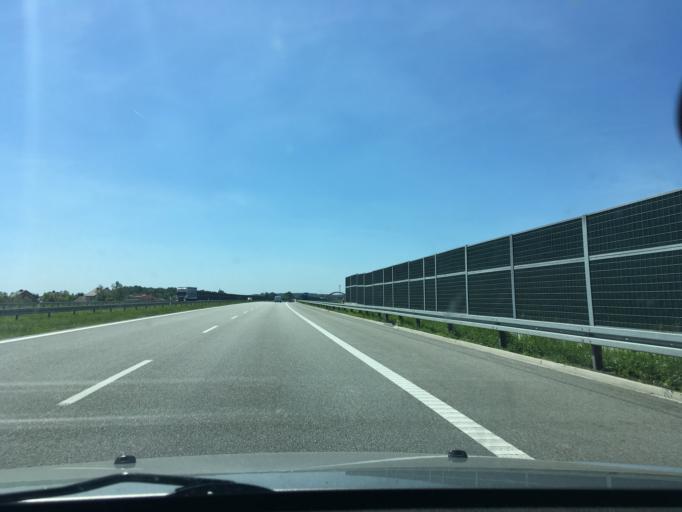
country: PL
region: Subcarpathian Voivodeship
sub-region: Powiat debicki
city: Zyrakow
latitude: 50.0808
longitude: 21.4032
